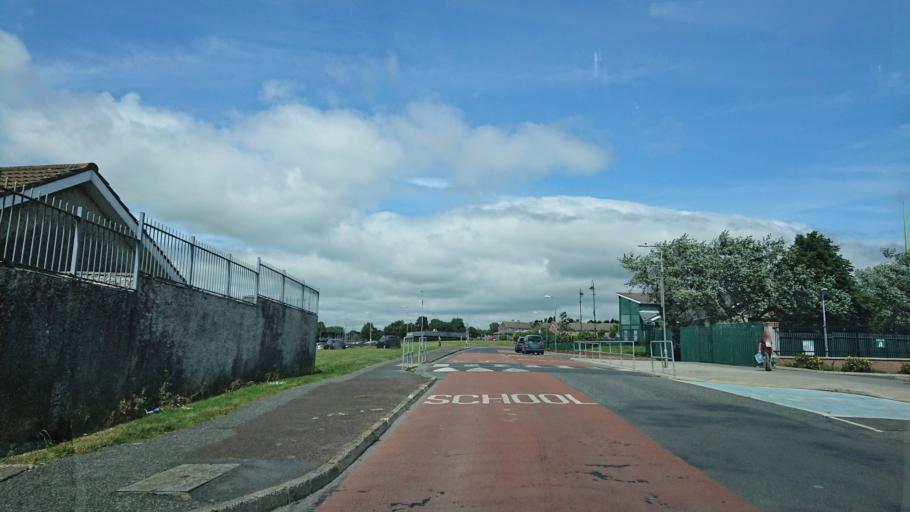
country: IE
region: Munster
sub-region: Waterford
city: Waterford
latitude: 52.2494
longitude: -7.1345
